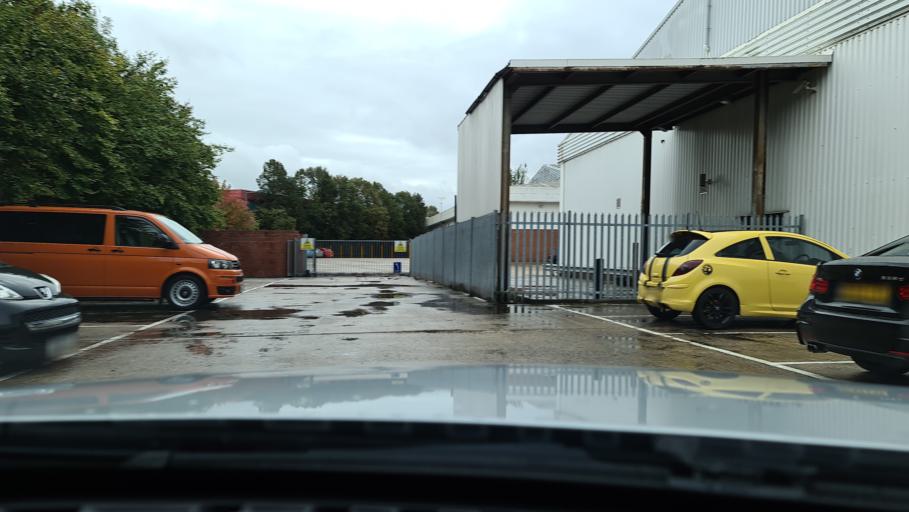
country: GB
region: England
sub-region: Buckinghamshire
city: Bletchley
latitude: 52.0039
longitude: -0.7244
